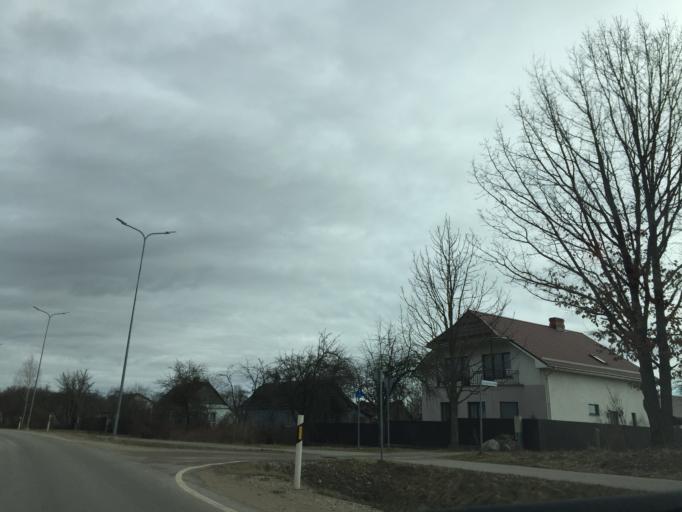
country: LV
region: Daugavpils
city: Daugavpils
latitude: 55.9044
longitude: 26.6483
